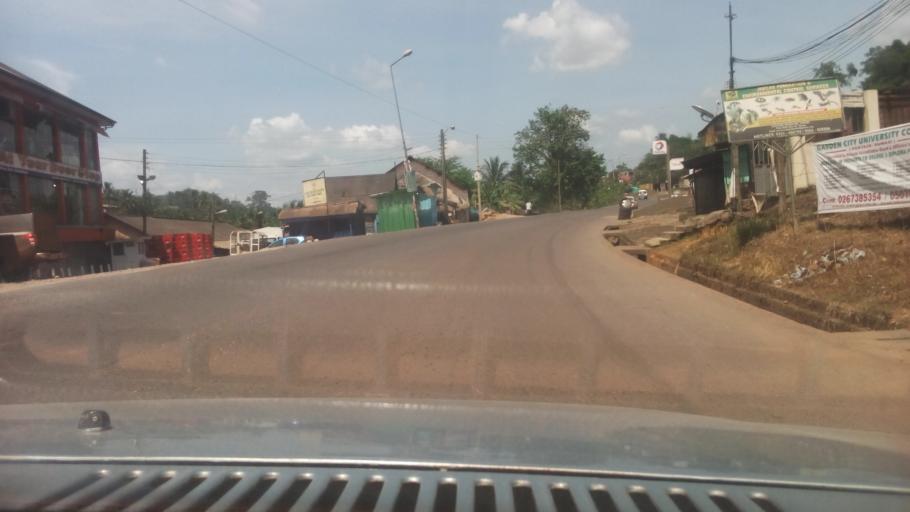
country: GH
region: Western
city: Tarkwa
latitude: 5.3084
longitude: -1.9941
